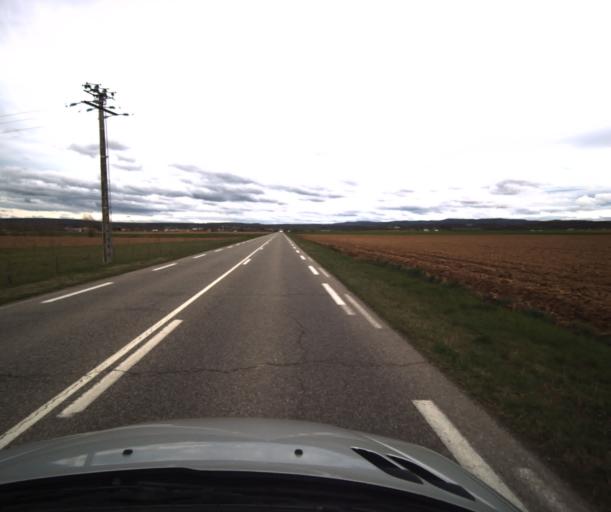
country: FR
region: Midi-Pyrenees
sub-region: Departement du Tarn-et-Garonne
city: Montricoux
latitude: 44.0737
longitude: 1.5804
